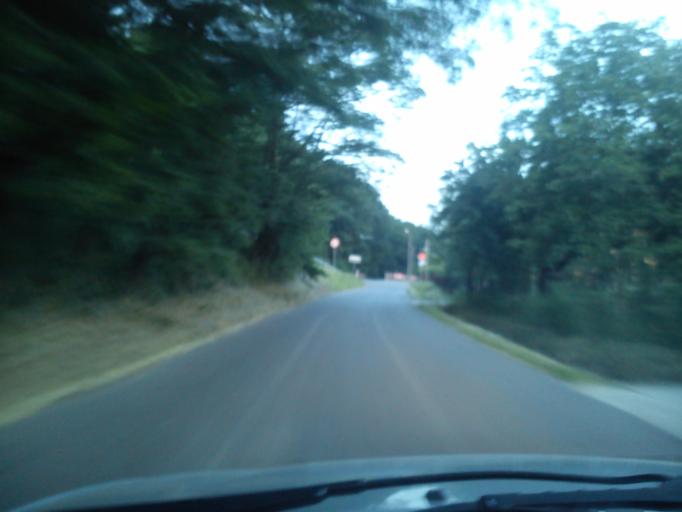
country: PL
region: Lesser Poland Voivodeship
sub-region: Powiat wielicki
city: Szarow
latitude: 50.0081
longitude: 20.2600
